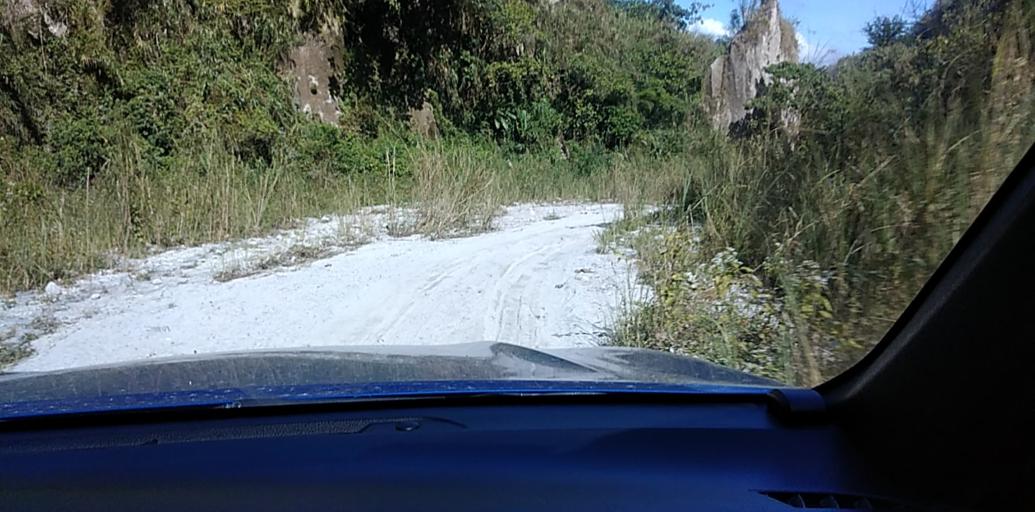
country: PH
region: Central Luzon
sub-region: Province of Pampanga
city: Dolores
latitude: 15.1641
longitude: 120.4720
